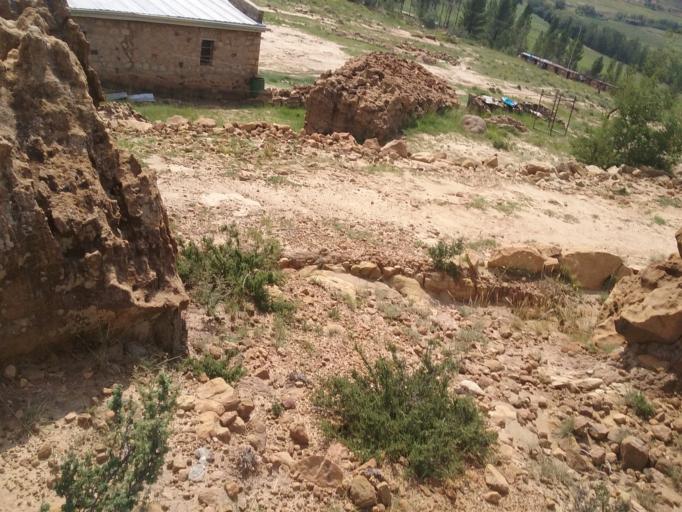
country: LS
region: Maseru
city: Maseru
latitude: -29.4255
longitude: 27.5763
